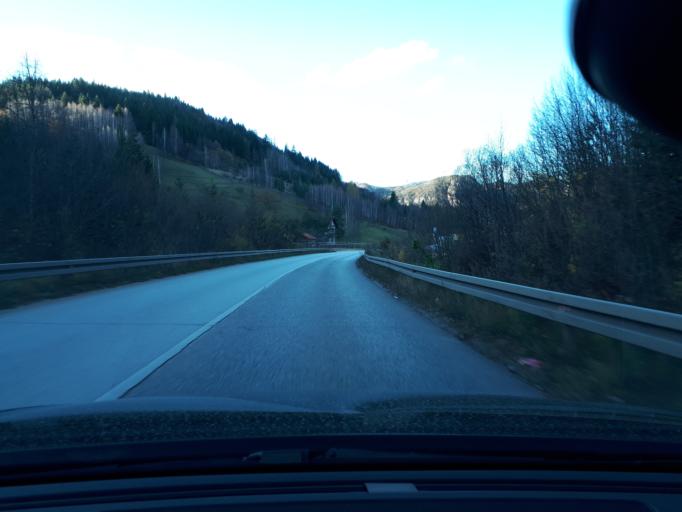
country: BA
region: Republika Srpska
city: Pale
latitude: 43.8401
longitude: 18.5532
